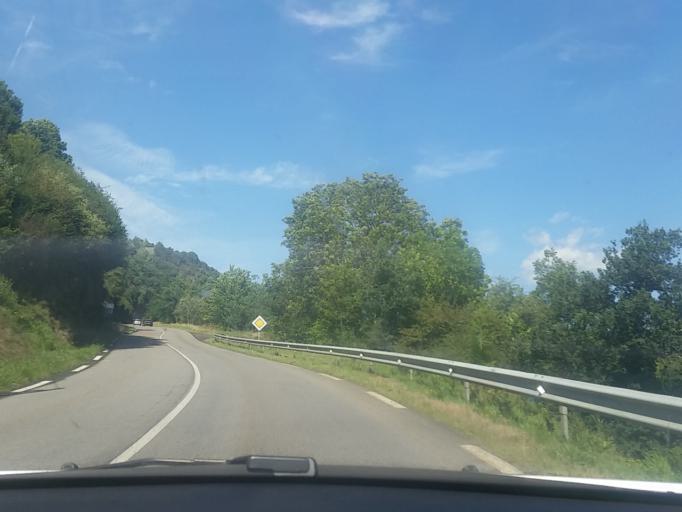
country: FR
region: Auvergne
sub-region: Departement du Cantal
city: Neuveglise
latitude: 44.8942
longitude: 3.0039
